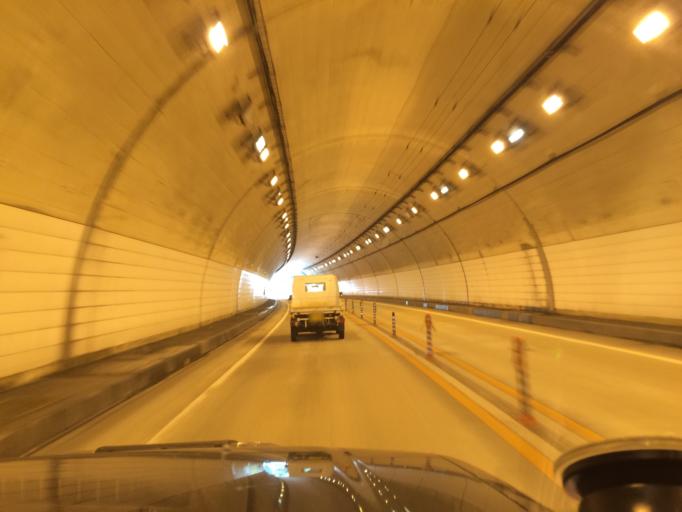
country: JP
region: Kyoto
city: Fukuchiyama
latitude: 35.1656
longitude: 135.0800
